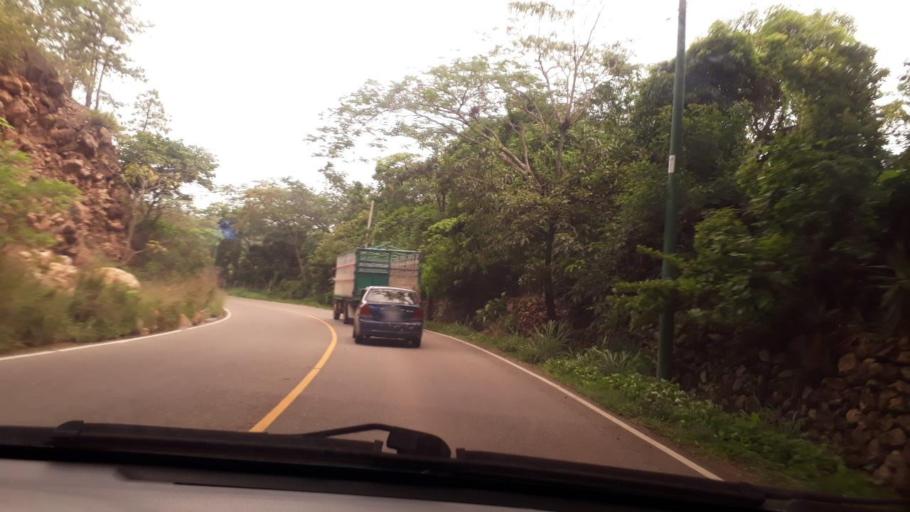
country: GT
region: Chiquimula
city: Concepcion Las Minas
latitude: 14.5639
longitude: -89.4527
